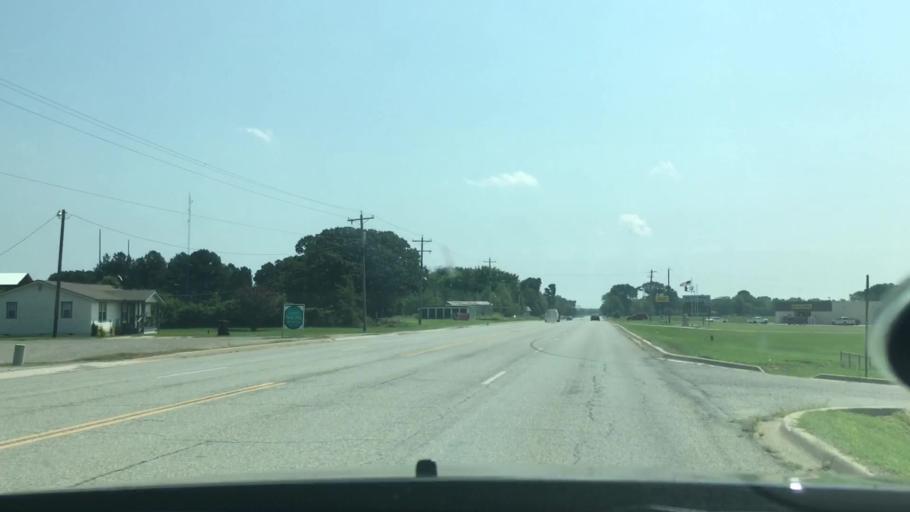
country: US
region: Oklahoma
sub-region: Atoka County
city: Atoka
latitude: 34.3022
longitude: -95.9967
